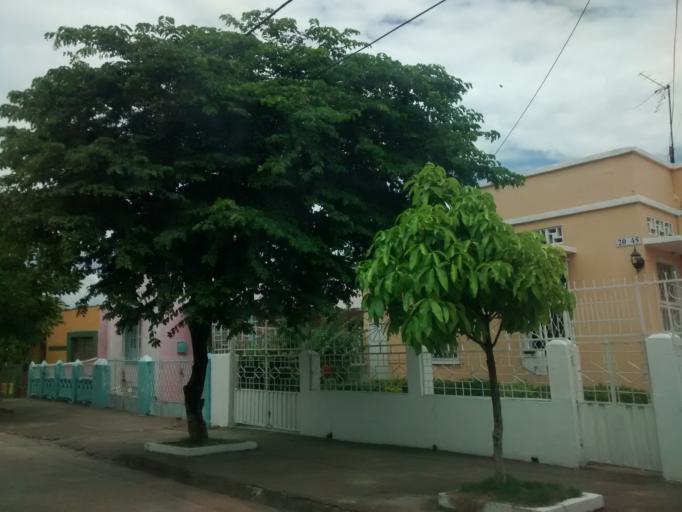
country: CO
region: Cundinamarca
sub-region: Girardot
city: Girardot City
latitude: 4.3028
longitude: -74.8103
